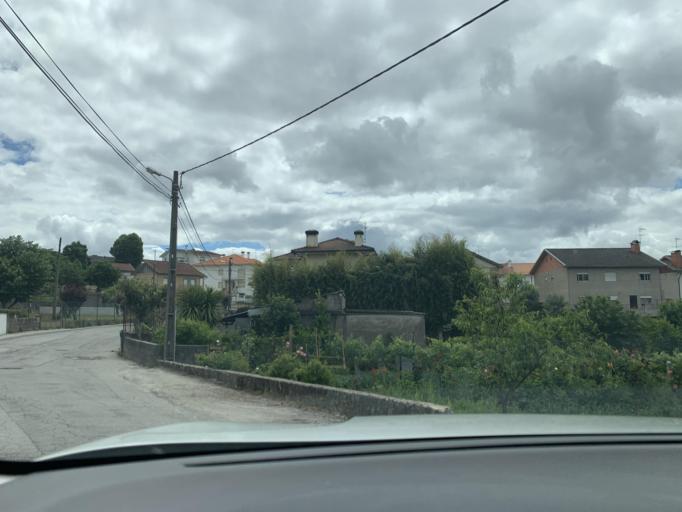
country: PT
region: Viseu
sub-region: Viseu
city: Abraveses
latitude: 40.6870
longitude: -7.9296
